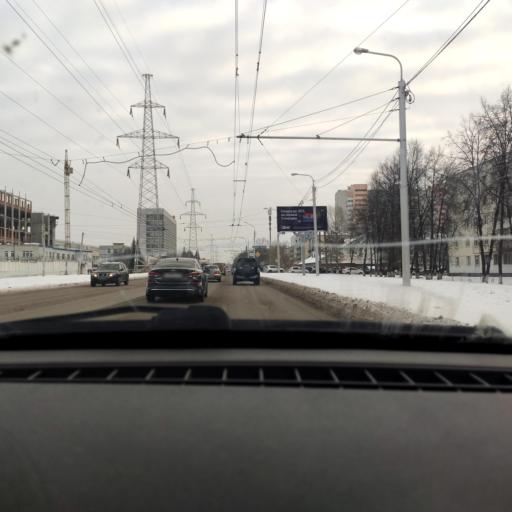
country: RU
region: Bashkortostan
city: Ufa
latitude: 54.7885
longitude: 56.1237
